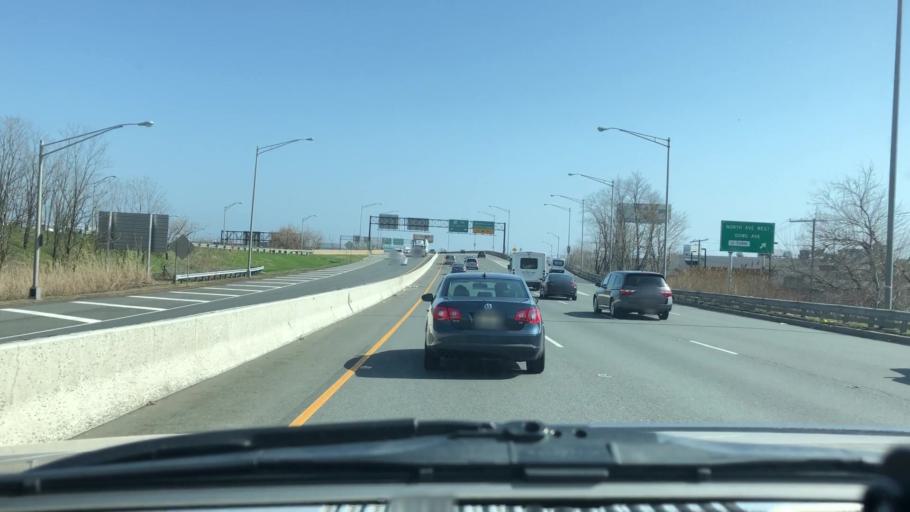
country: US
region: New Jersey
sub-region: Union County
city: Elizabeth
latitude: 40.6791
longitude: -74.1928
